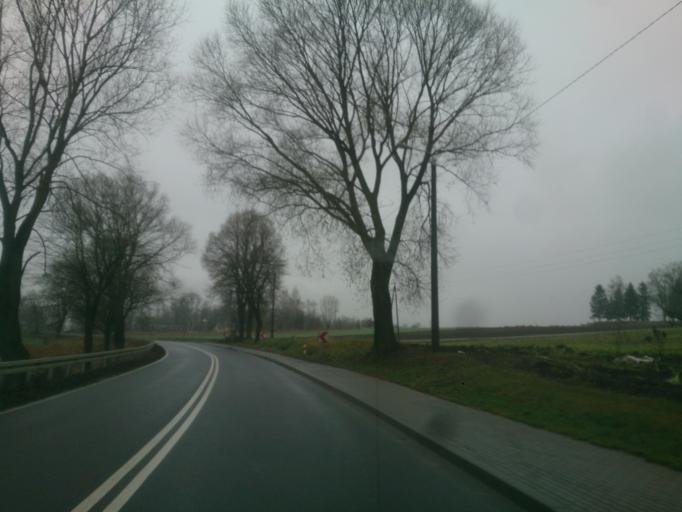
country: PL
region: Kujawsko-Pomorskie
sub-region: Powiat rypinski
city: Rypin
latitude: 53.1236
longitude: 19.3864
